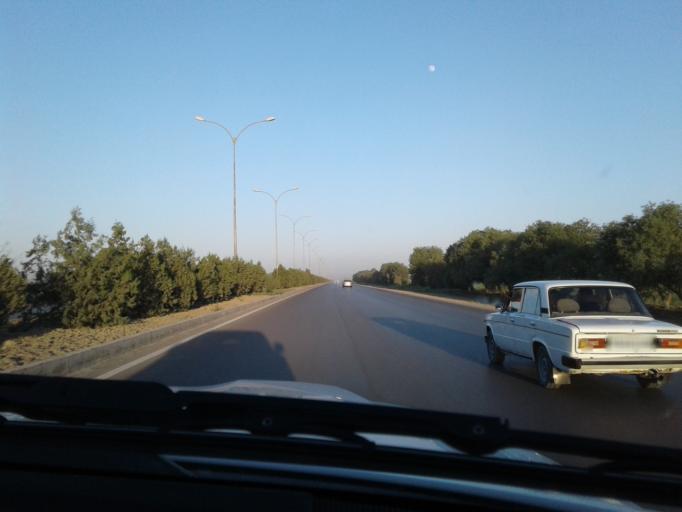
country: TM
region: Ahal
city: Abadan
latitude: 38.1330
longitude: 58.0181
